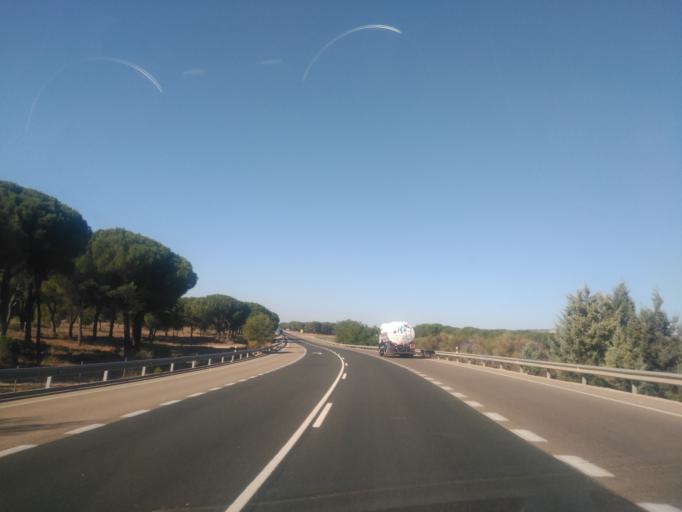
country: ES
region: Castille and Leon
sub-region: Provincia de Valladolid
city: Quintanilla de Onesimo
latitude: 41.6215
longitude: -4.3802
